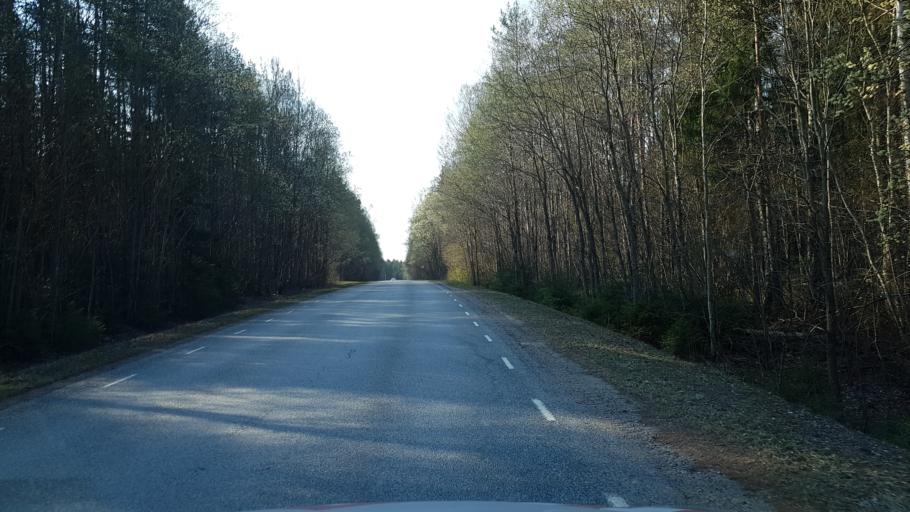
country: EE
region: Raplamaa
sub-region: Kohila vald
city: Kohila
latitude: 59.1787
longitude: 24.6559
